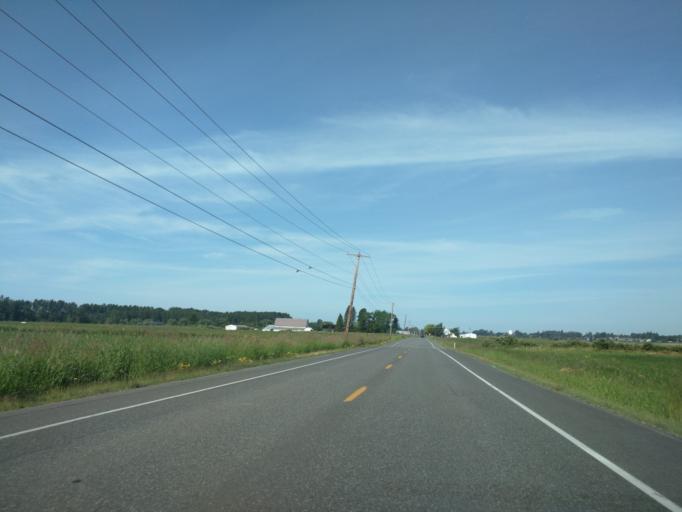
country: US
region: Washington
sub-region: Whatcom County
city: Lynden
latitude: 48.9421
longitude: -122.4012
